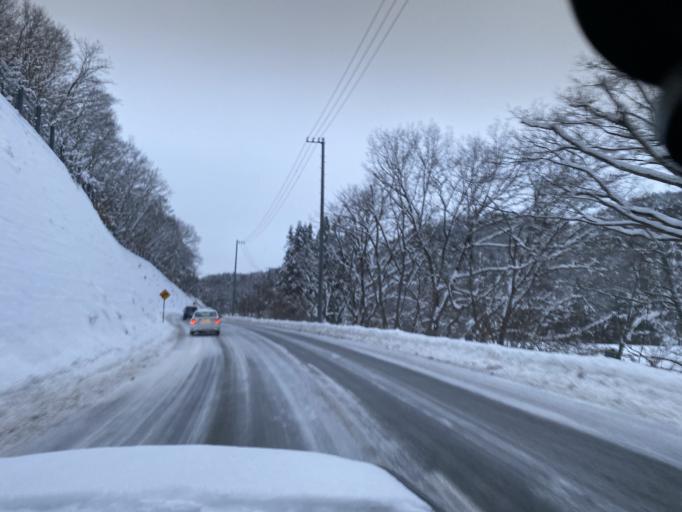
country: JP
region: Nagano
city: Omachi
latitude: 36.5370
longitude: 137.8643
